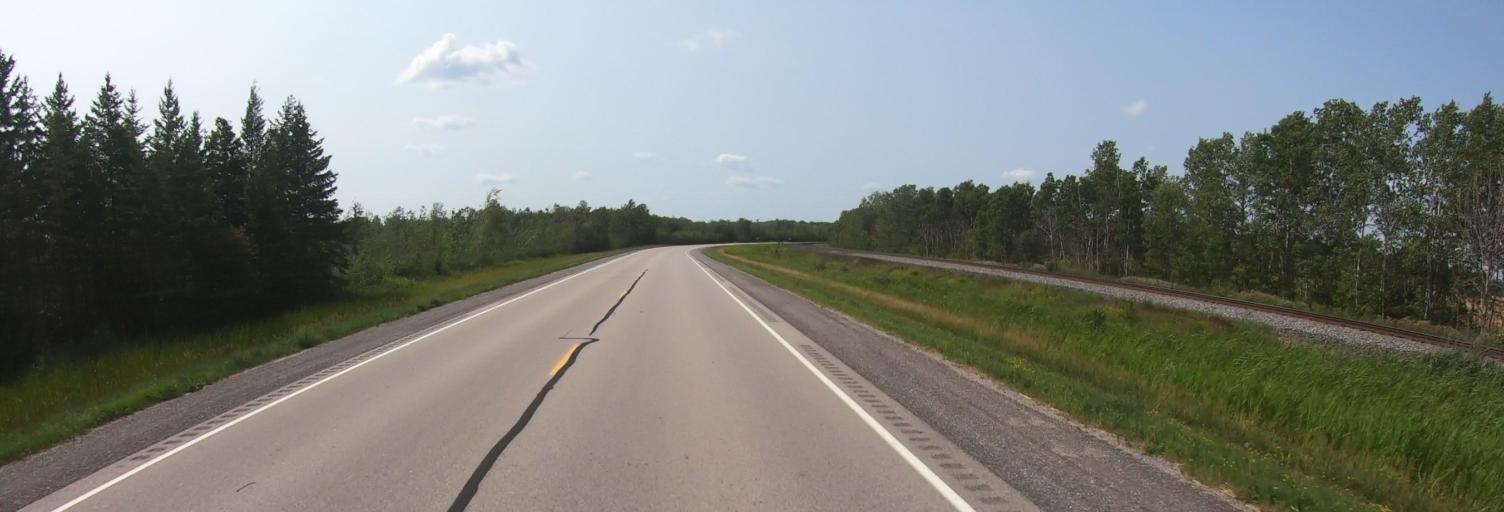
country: US
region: Minnesota
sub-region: Lake of the Woods County
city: Baudette
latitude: 48.7106
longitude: -94.7052
